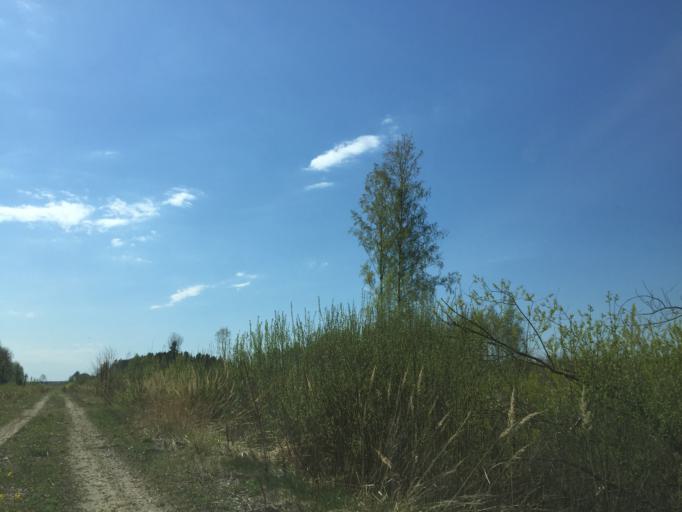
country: LV
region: Saulkrastu
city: Saulkrasti
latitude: 57.3463
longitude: 24.4848
